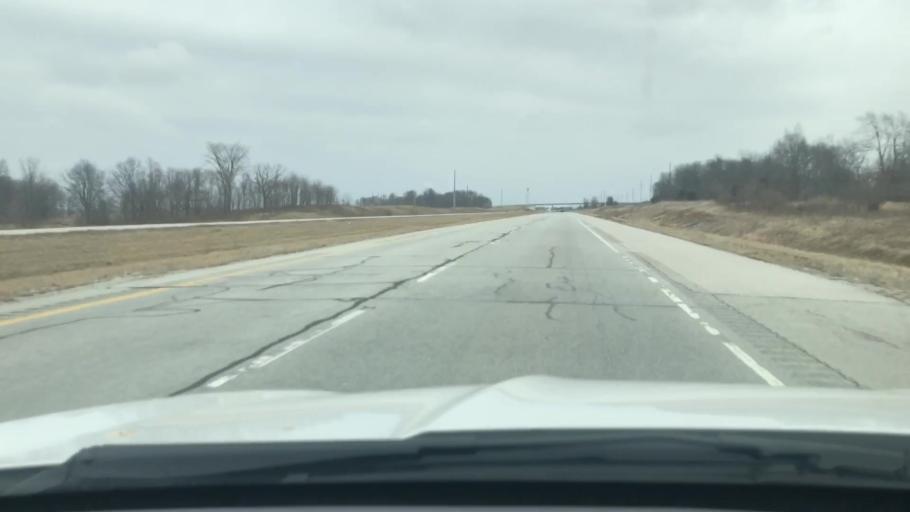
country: US
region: Indiana
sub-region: Cass County
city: Georgetown
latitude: 40.6544
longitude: -86.5503
